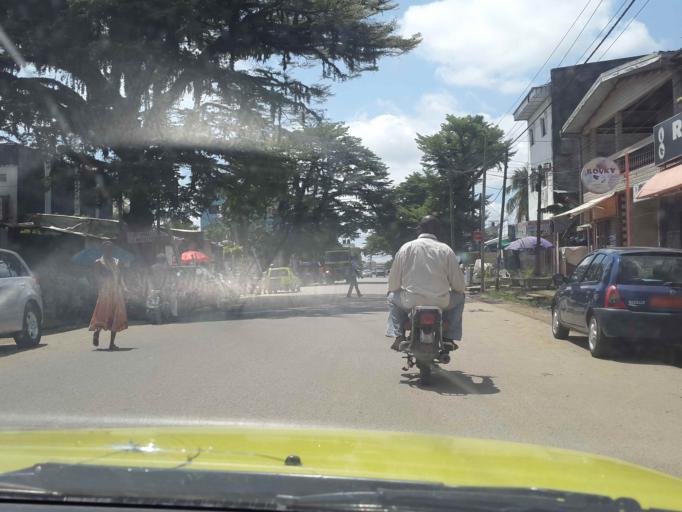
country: CM
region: Littoral
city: Douala
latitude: 4.0870
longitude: 9.7412
